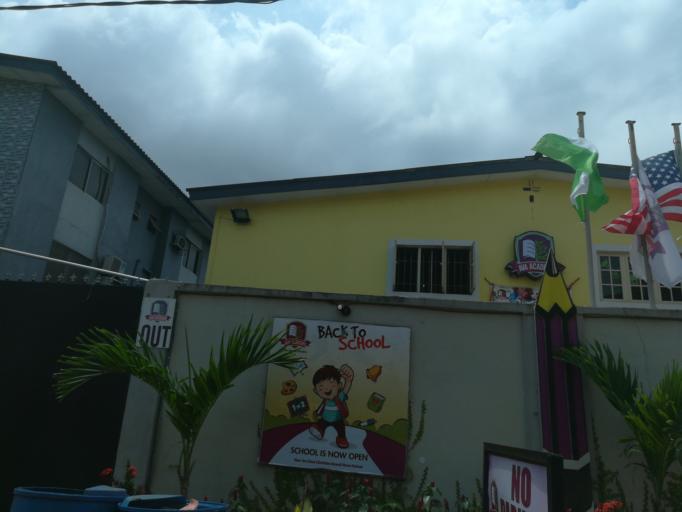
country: NG
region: Lagos
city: Oshodi
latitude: 6.5493
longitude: 3.3271
